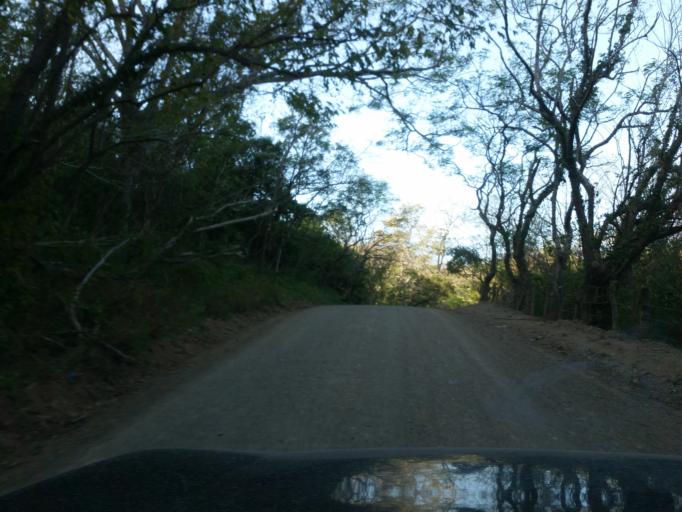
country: NI
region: Rivas
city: San Juan del Sur
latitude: 11.2148
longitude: -85.8120
